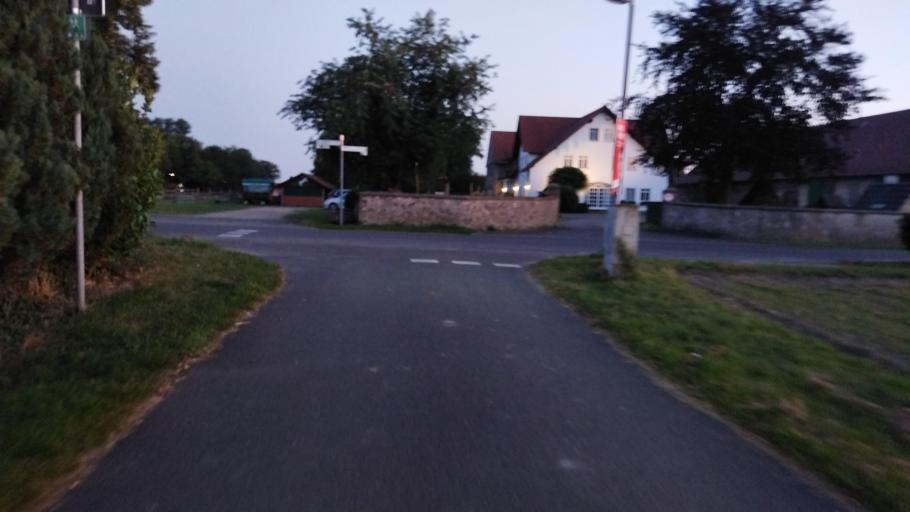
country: DE
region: Lower Saxony
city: Bad Laer
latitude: 52.0950
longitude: 8.0915
